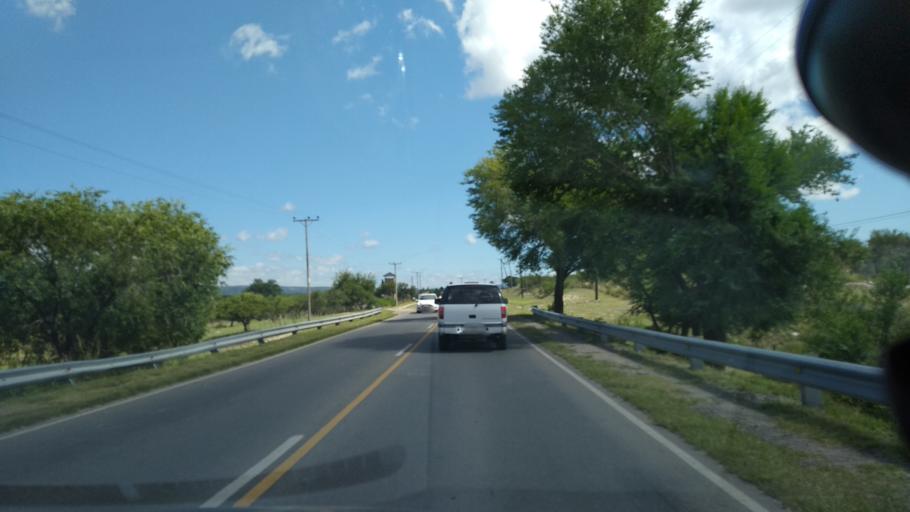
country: AR
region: Cordoba
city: Mina Clavero
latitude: -31.7793
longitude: -64.9999
